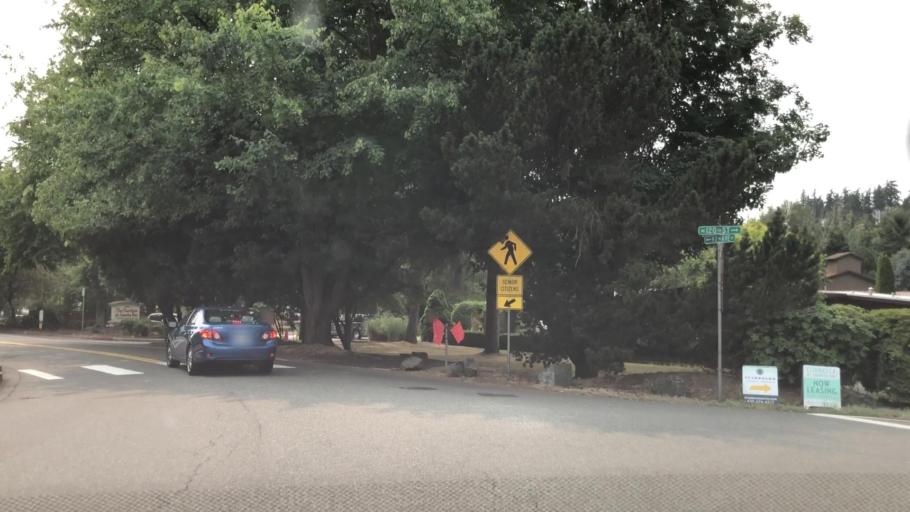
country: US
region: Washington
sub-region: King County
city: Inglewood-Finn Hill
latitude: 47.7073
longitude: -122.2124
